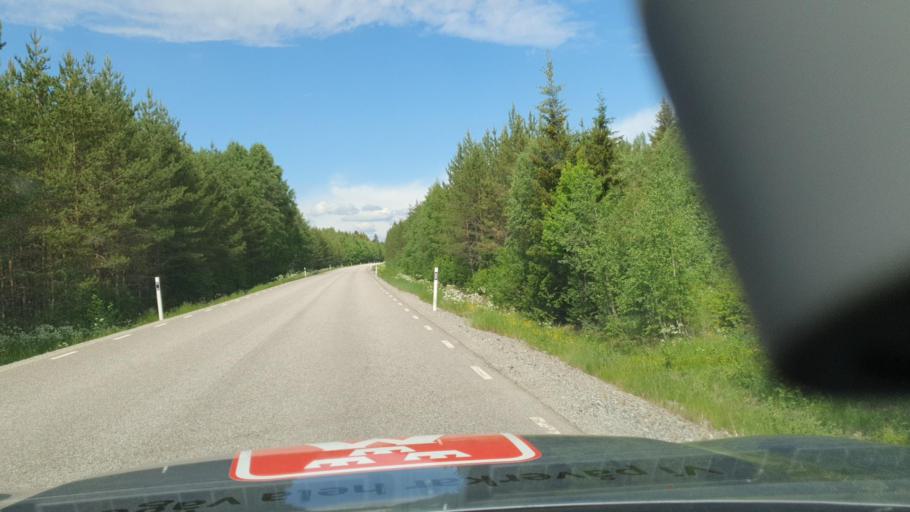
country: SE
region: Vaesternorrland
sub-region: Kramfors Kommun
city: Kramfors
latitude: 63.0393
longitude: 17.8086
